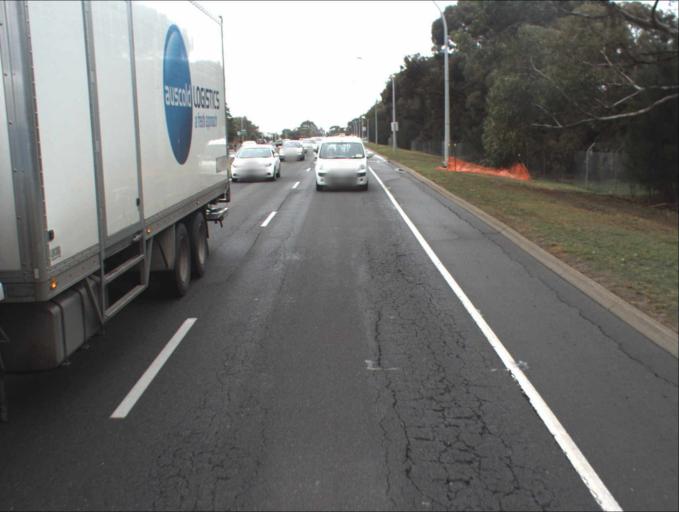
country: AU
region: South Australia
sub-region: Port Adelaide Enfield
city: Gilles Plains
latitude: -34.8495
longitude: 138.6498
